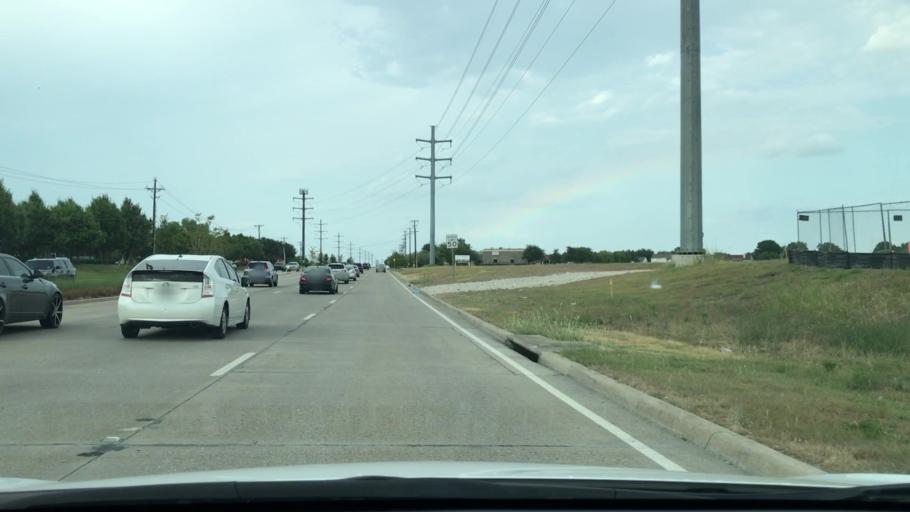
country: US
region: Texas
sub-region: Dallas County
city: Rowlett
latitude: 32.9112
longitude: -96.5302
